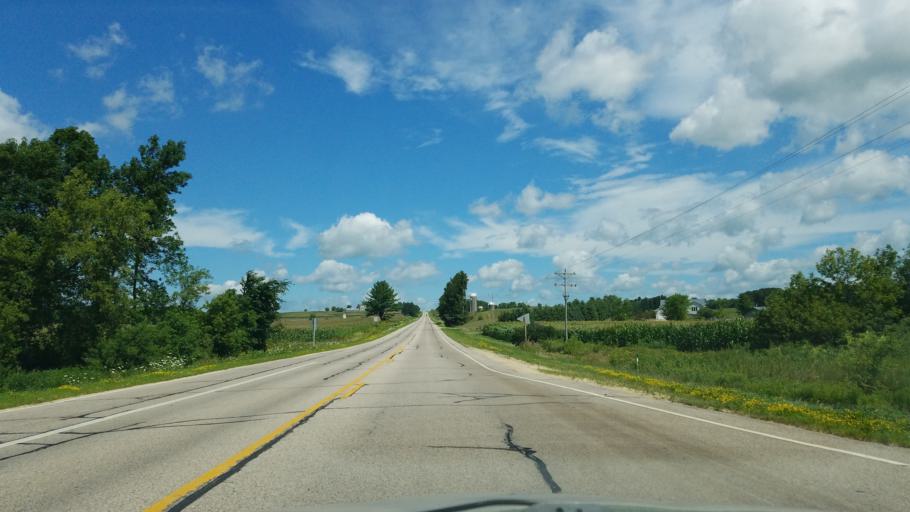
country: US
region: Wisconsin
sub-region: Saint Croix County
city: Glenwood City
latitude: 45.0026
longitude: -92.1967
